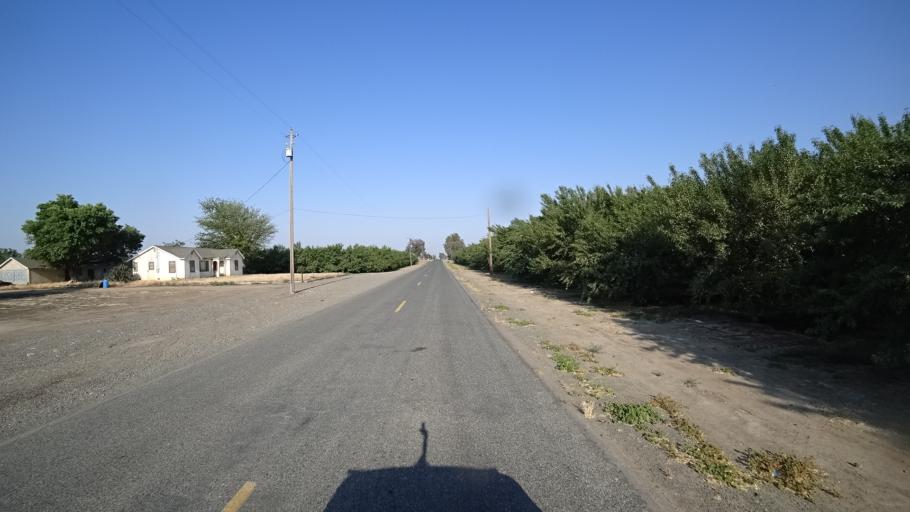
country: US
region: California
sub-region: Fresno County
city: Riverdale
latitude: 36.3803
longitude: -119.8133
